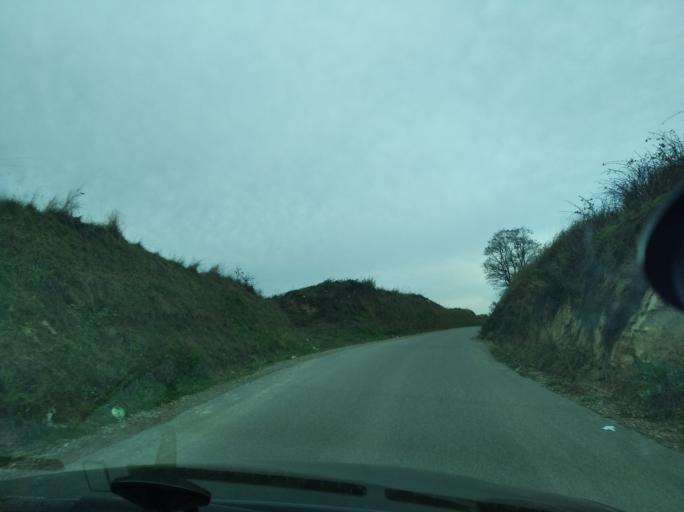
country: PL
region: Subcarpathian Voivodeship
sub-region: Powiat przeworski
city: Grzeska
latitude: 50.0669
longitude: 22.4638
